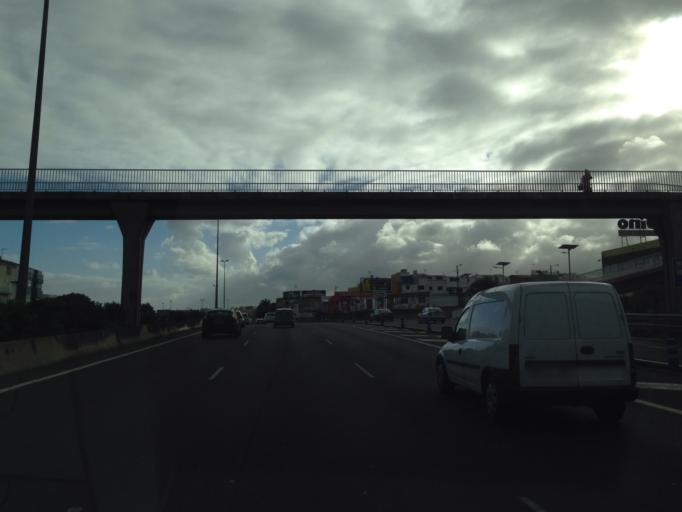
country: ES
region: Canary Islands
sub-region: Provincia de Las Palmas
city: Telde
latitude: 28.0044
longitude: -15.3914
